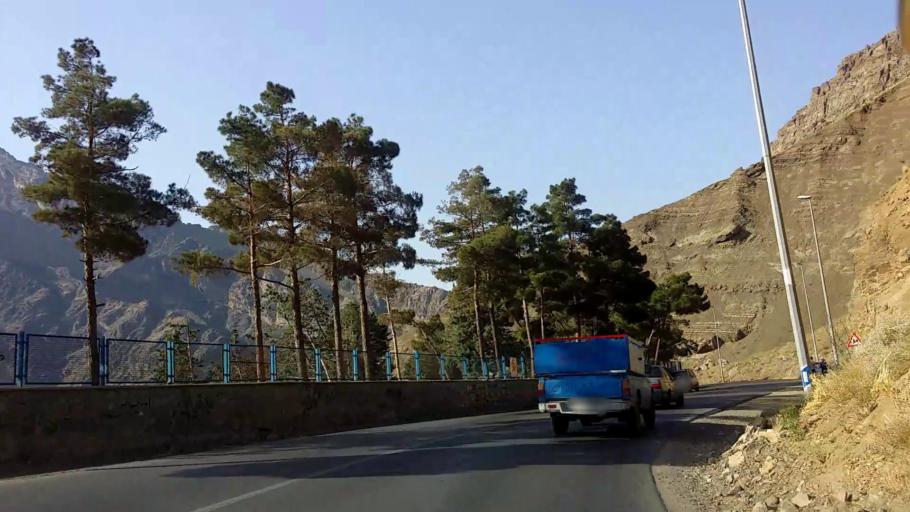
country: IR
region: Alborz
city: Karaj
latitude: 35.9703
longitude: 51.0939
